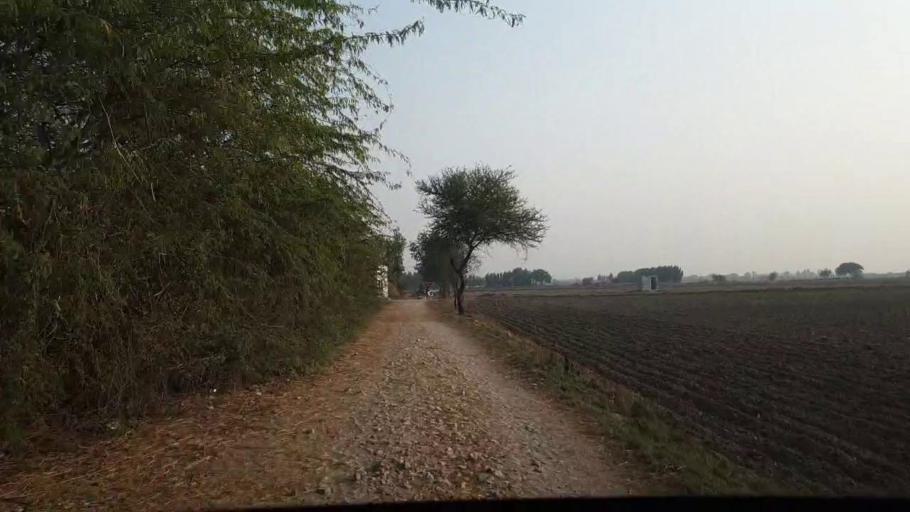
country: PK
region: Sindh
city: Chuhar Jamali
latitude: 24.2552
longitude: 68.1137
